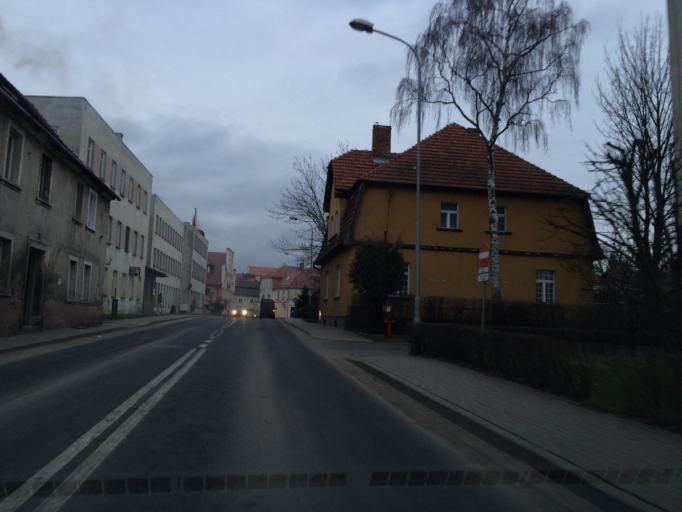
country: PL
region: Lower Silesian Voivodeship
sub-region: Powiat boleslawiecki
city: Nowogrodziec
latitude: 51.1961
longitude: 15.3949
